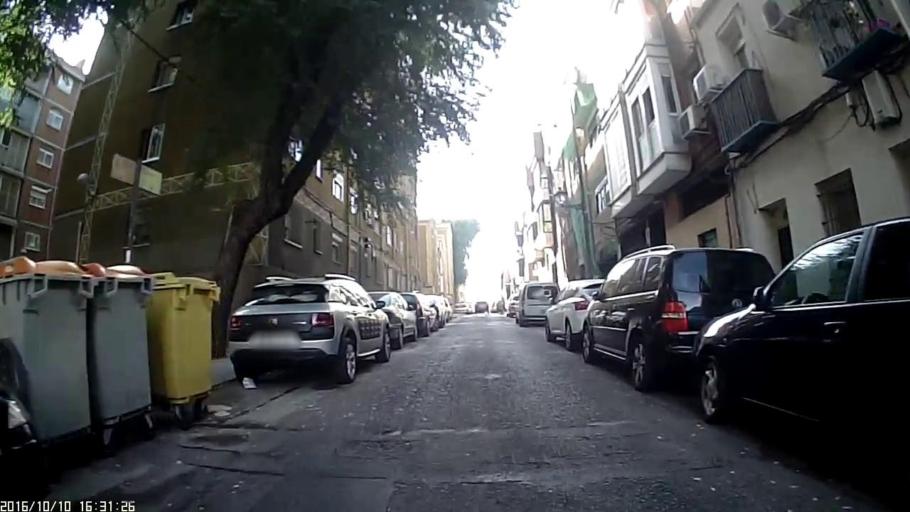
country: ES
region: Madrid
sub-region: Provincia de Madrid
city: Carabanchel
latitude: 40.4119
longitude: -3.7254
